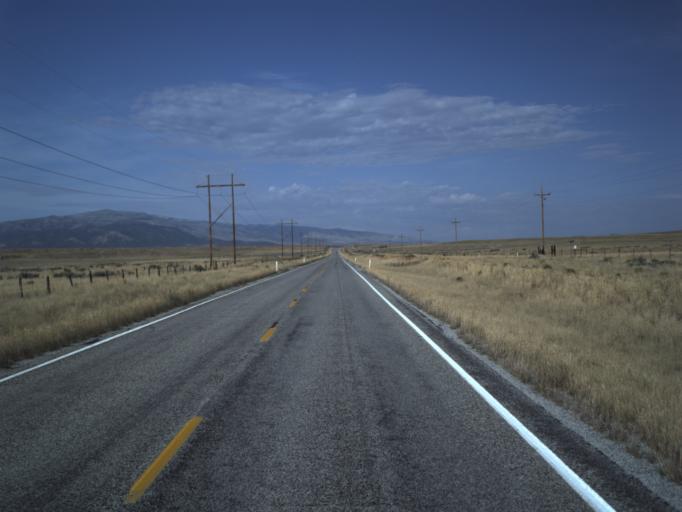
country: US
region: Idaho
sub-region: Oneida County
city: Malad City
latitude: 41.9655
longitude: -113.0376
